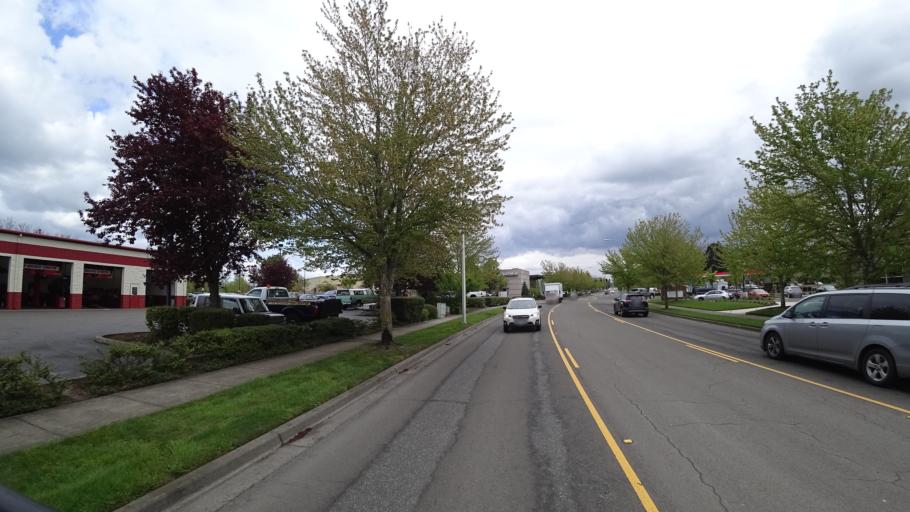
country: US
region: Oregon
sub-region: Washington County
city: Rockcreek
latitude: 45.5501
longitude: -122.9059
